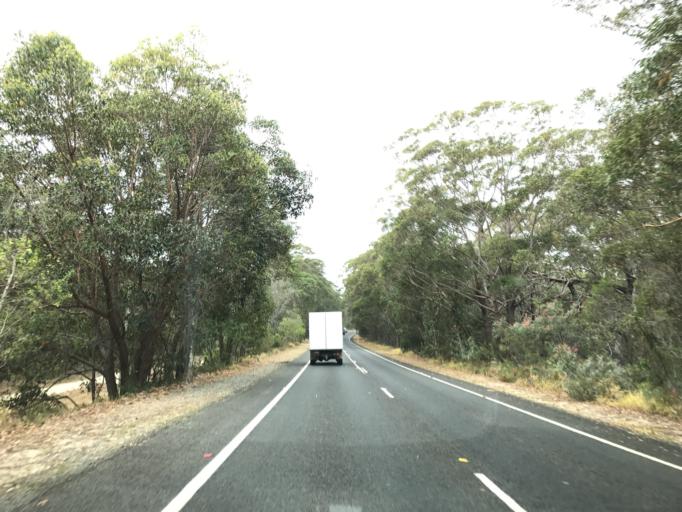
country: AU
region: Queensland
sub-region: Redland
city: Victoria Point
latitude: -27.4376
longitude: 153.4939
